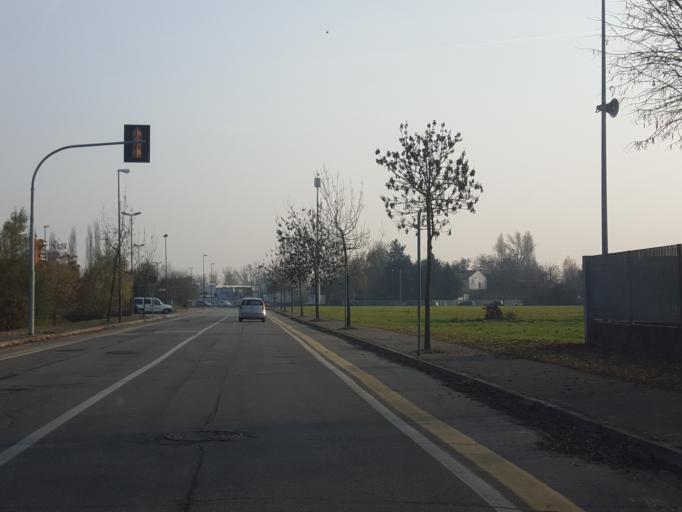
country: IT
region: Veneto
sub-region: Provincia di Treviso
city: Treviso
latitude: 45.6705
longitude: 12.2168
